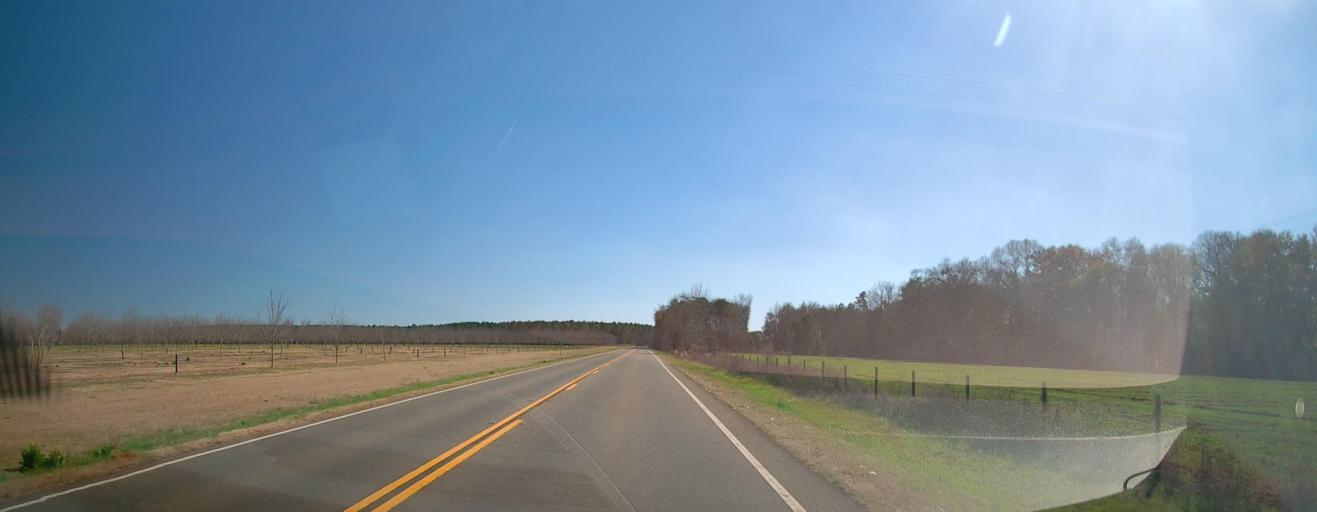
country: US
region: Georgia
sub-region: Macon County
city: Montezuma
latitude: 32.3732
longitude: -84.0141
